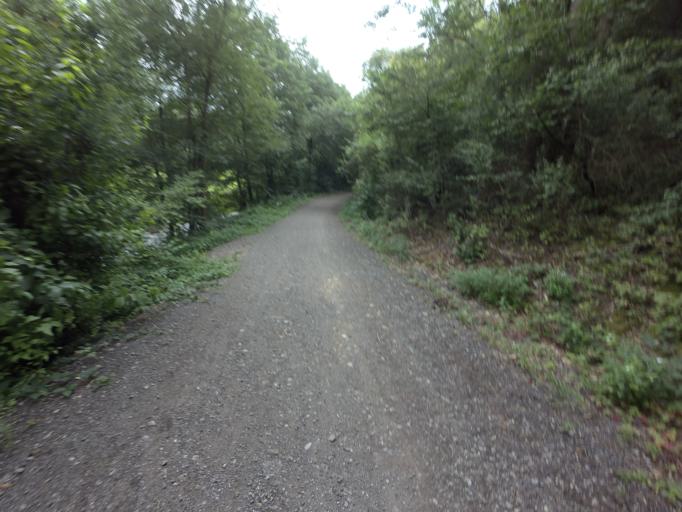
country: BE
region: Wallonia
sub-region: Province de Liege
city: Plombieres
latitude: 50.7260
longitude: 5.9758
